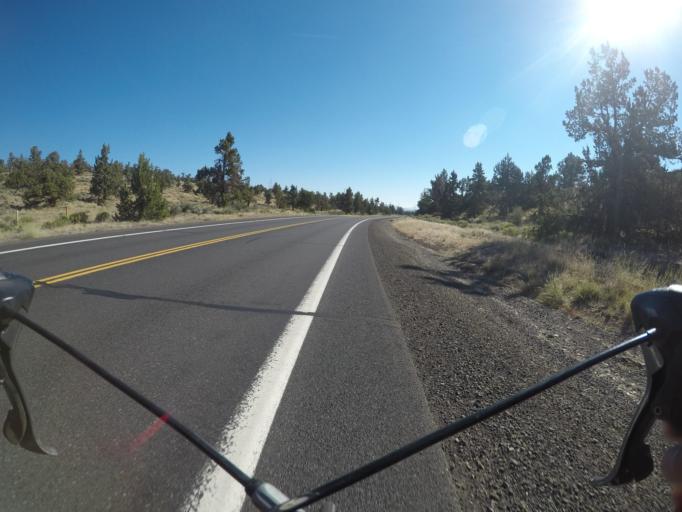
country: US
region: Oregon
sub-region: Deschutes County
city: Redmond
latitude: 44.2515
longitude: -121.2752
